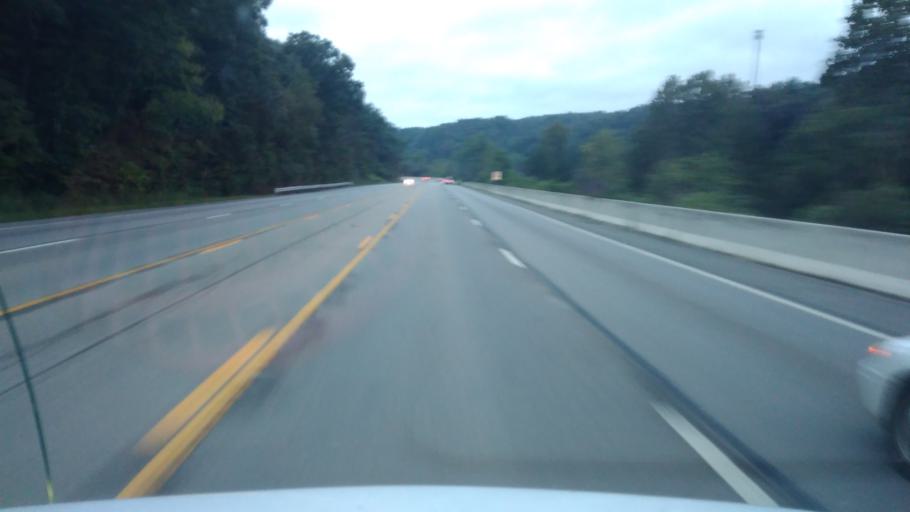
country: US
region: Ohio
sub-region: Pike County
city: Waverly
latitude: 39.2102
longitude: -82.9835
